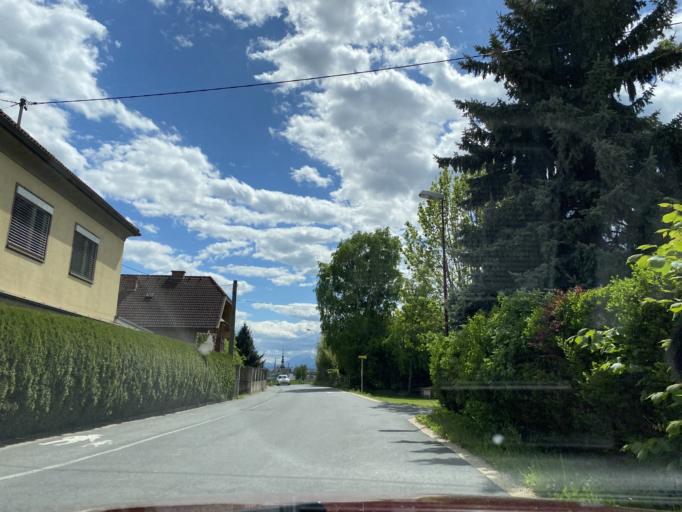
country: AT
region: Carinthia
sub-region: Politischer Bezirk Wolfsberg
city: Wolfsberg
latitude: 46.8500
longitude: 14.8403
